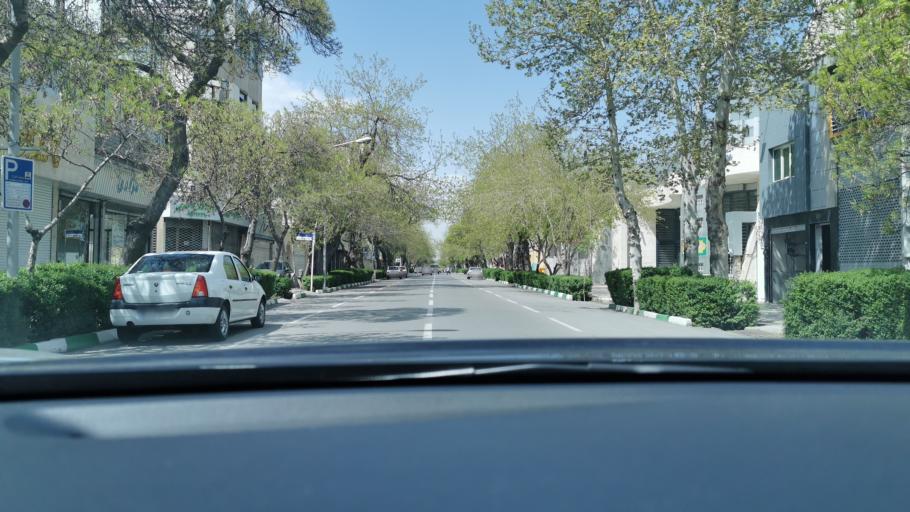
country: IR
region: Razavi Khorasan
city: Mashhad
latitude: 36.2972
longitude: 59.5949
